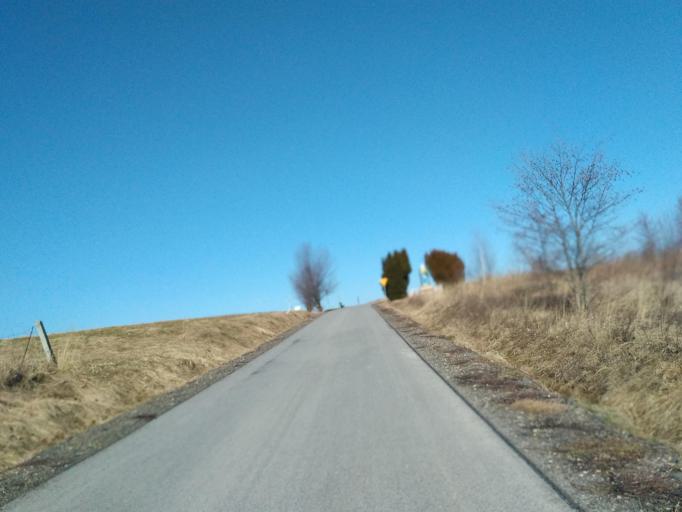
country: PL
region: Subcarpathian Voivodeship
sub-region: Powiat rzeszowski
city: Lubenia
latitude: 49.9352
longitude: 21.9441
